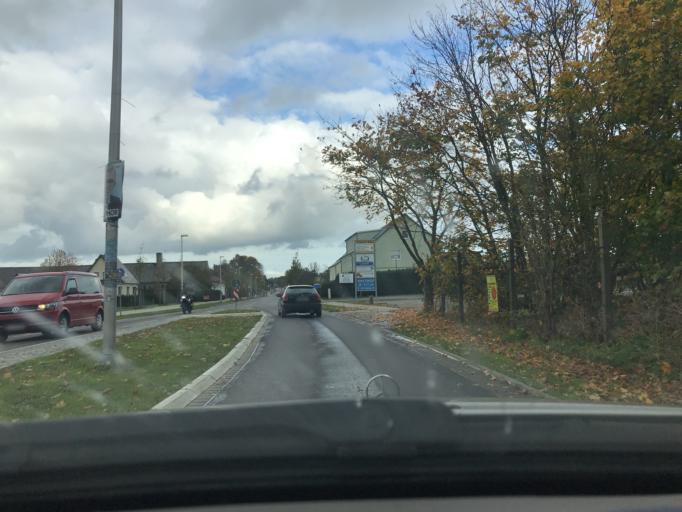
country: DE
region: Mecklenburg-Vorpommern
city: Zussow
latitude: 53.9724
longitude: 13.5419
